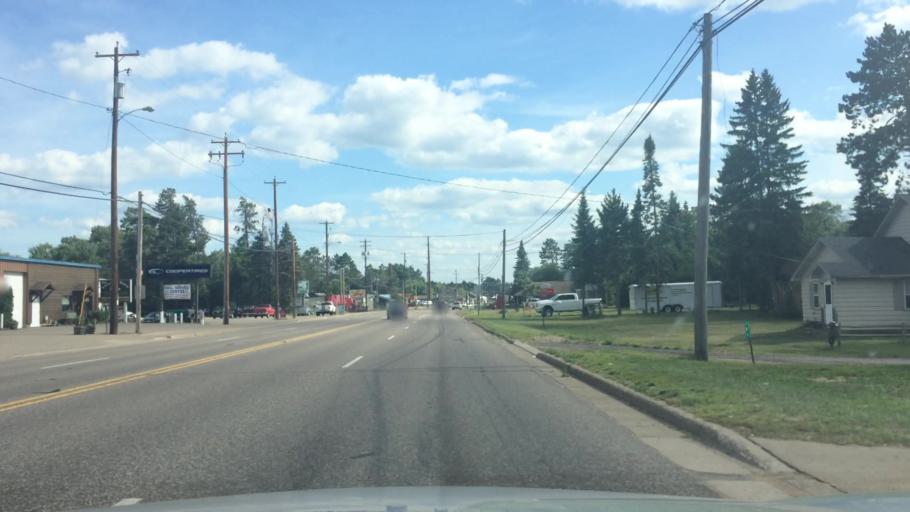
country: US
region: Wisconsin
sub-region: Vilas County
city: Lac du Flambeau
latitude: 45.9018
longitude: -89.6977
